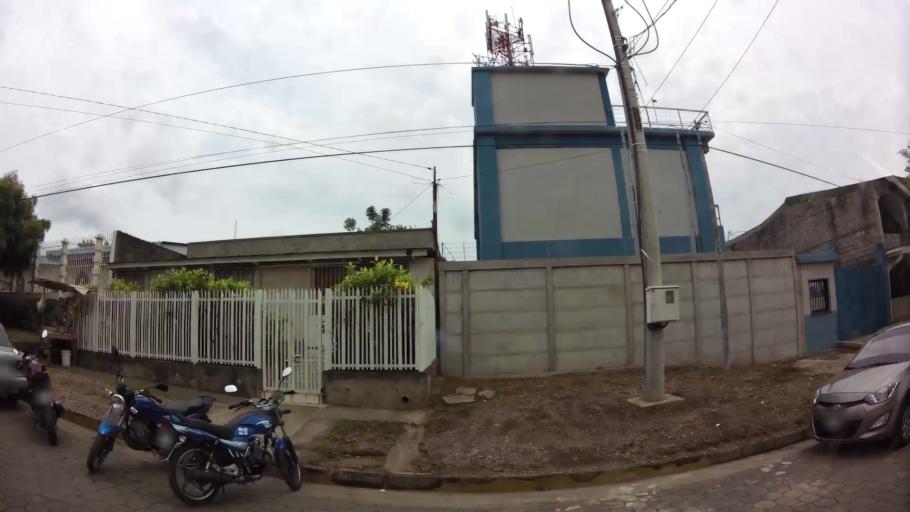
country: NI
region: Granada
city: Granada
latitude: 11.9331
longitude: -85.9643
